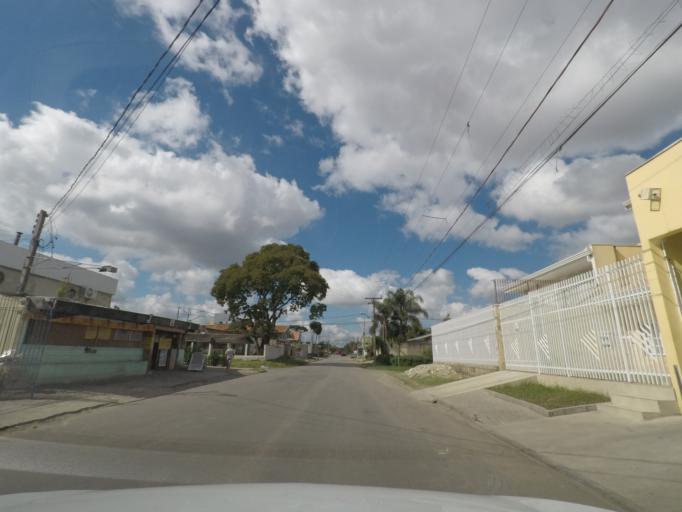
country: BR
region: Parana
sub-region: Sao Jose Dos Pinhais
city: Sao Jose dos Pinhais
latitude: -25.4895
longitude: -49.2294
